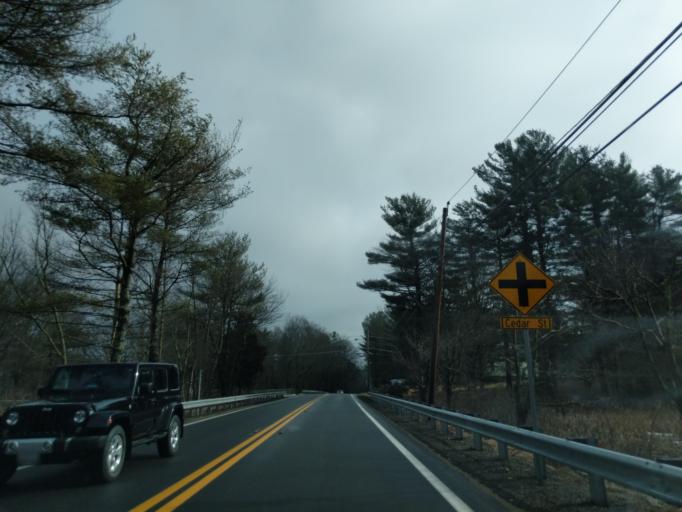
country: US
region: Massachusetts
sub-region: Worcester County
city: Douglas
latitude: 42.0553
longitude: -71.7697
